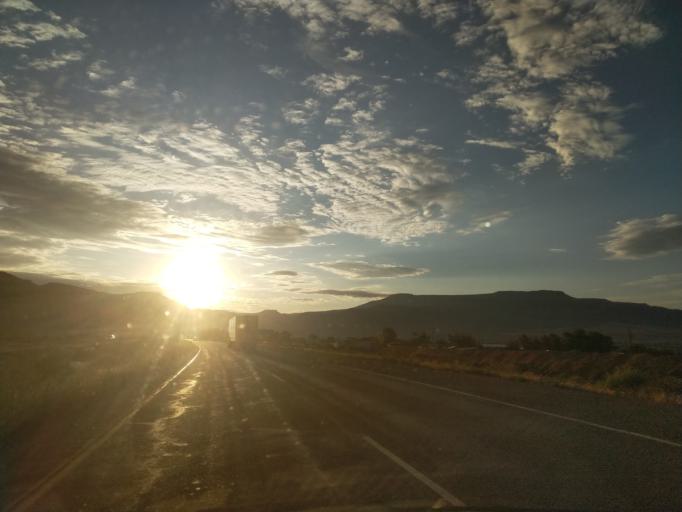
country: US
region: Colorado
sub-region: Mesa County
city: Clifton
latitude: 39.1077
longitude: -108.4290
